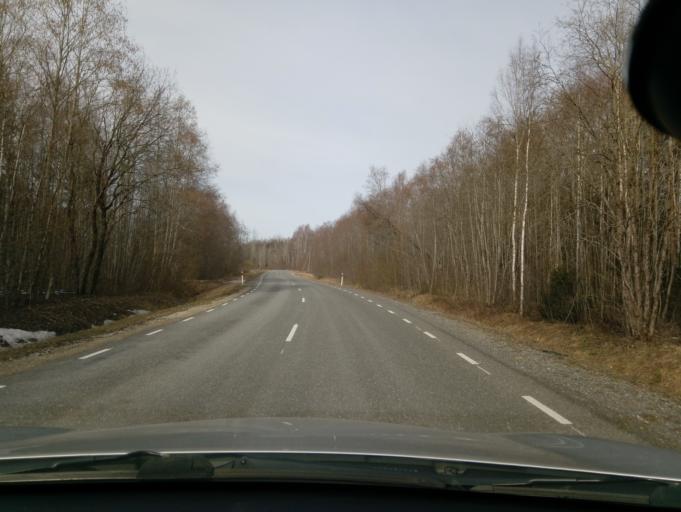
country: EE
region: Jaervamaa
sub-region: Tueri vald
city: Tueri
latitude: 58.8241
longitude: 25.3687
